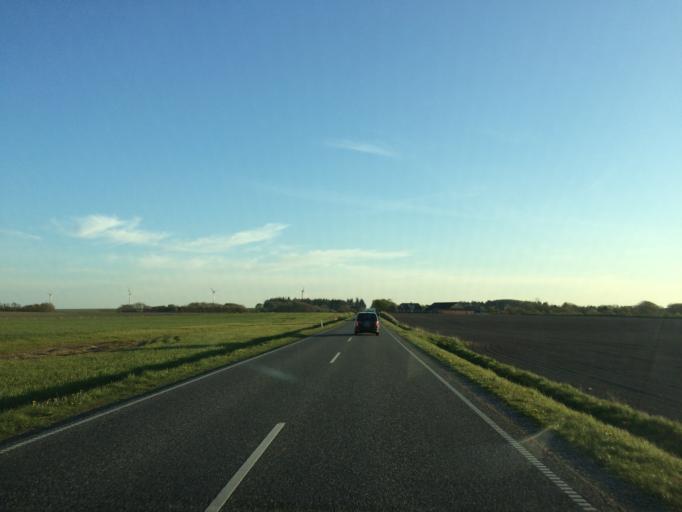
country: DK
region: Central Jutland
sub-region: Struer Kommune
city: Struer
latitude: 56.4367
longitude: 8.5237
